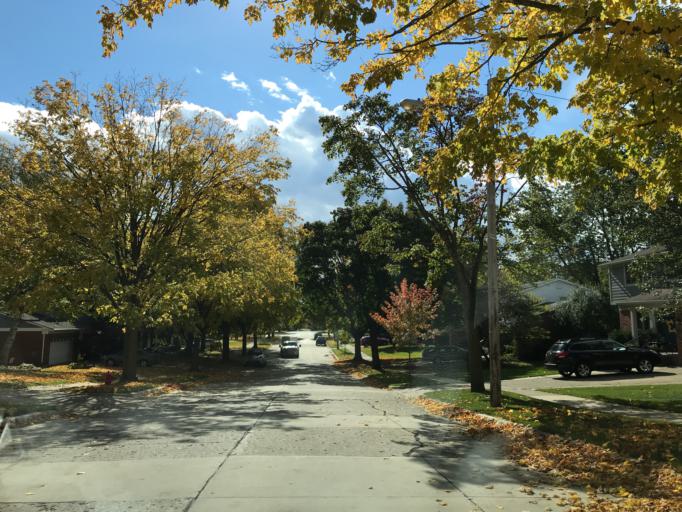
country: US
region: Michigan
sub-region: Washtenaw County
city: Ann Arbor
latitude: 42.2513
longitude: -83.7132
